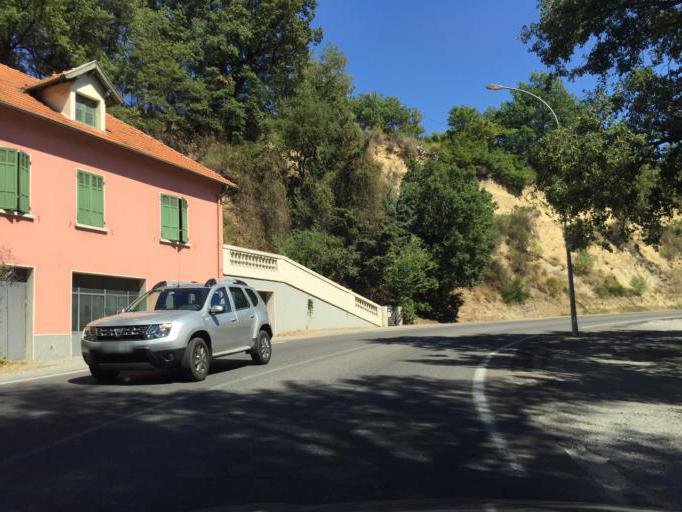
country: FR
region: Provence-Alpes-Cote d'Azur
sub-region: Departement des Alpes-de-Haute-Provence
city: Volonne
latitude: 44.0797
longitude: 5.9944
